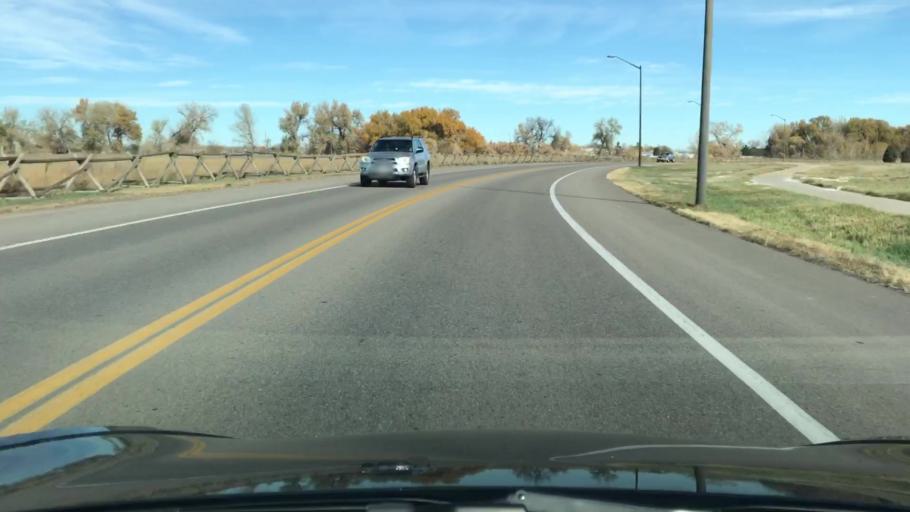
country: US
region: Colorado
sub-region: Larimer County
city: Fort Collins
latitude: 40.5755
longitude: -105.0391
